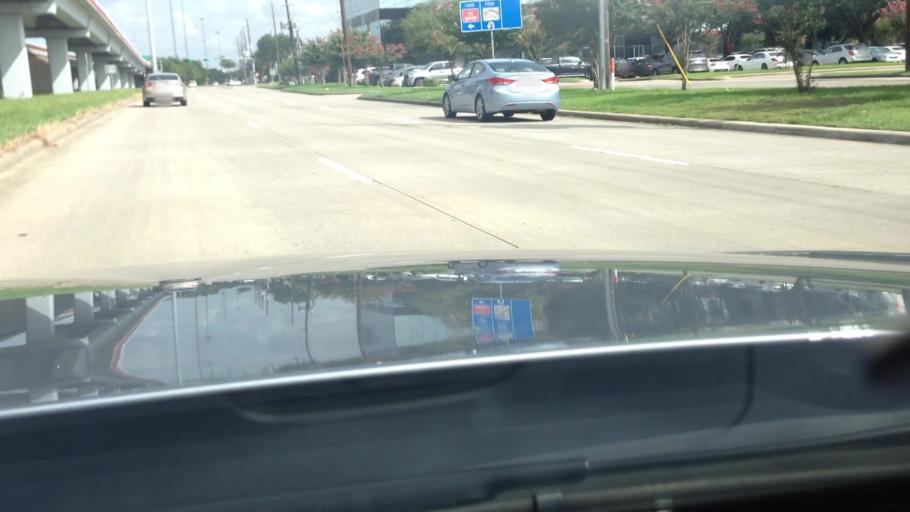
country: US
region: Texas
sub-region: Harris County
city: Hudson
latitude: 29.9558
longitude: -95.5407
